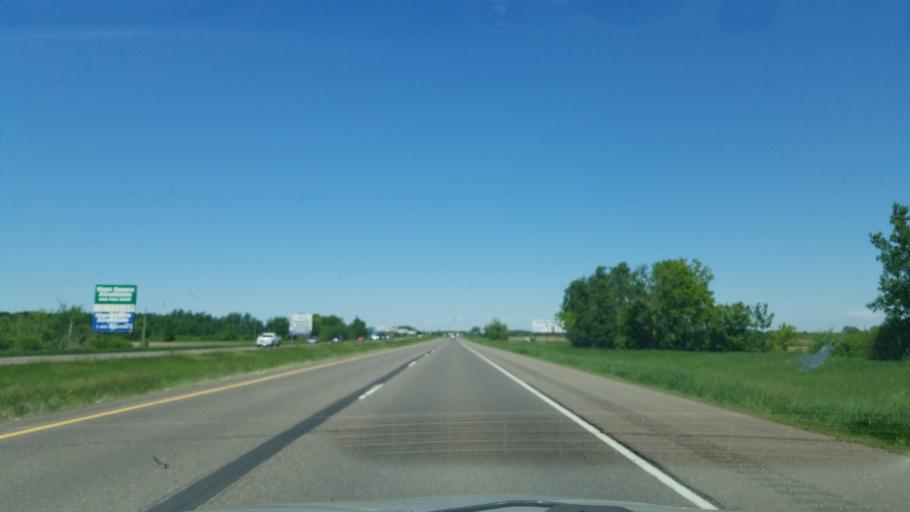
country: US
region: Minnesota
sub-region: Pine County
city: Rock Creek
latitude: 45.7337
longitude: -92.9918
